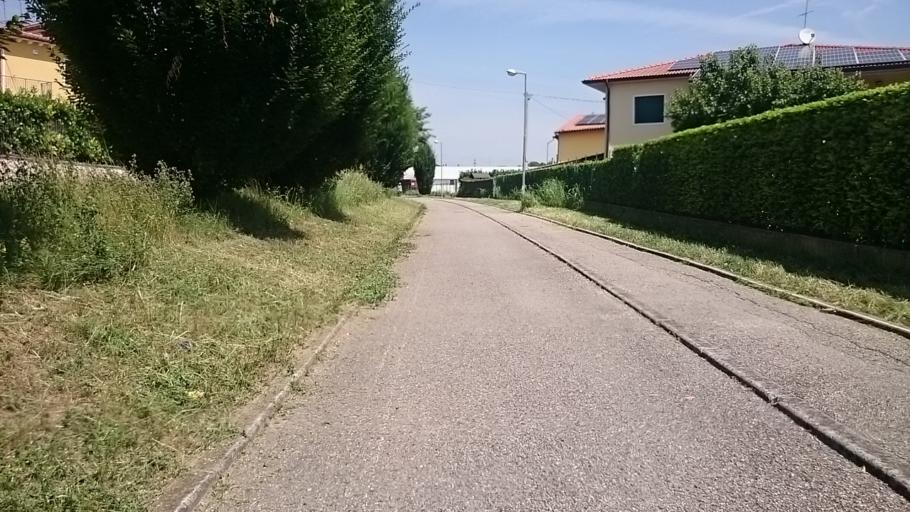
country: IT
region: Veneto
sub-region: Provincia di Vicenza
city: Longare
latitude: 45.4740
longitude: 11.6103
